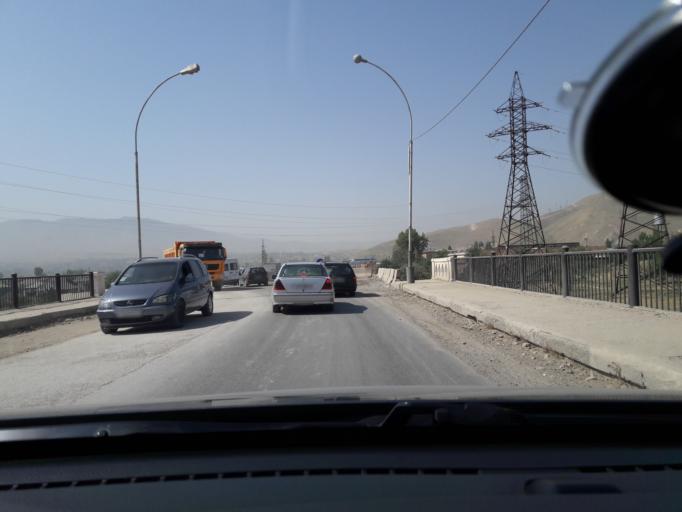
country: TJ
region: Dushanbe
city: Boshkengash
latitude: 38.4571
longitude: 68.7361
